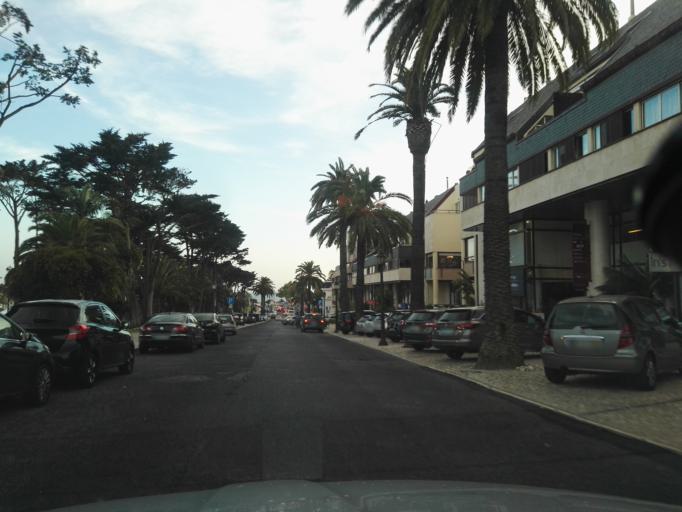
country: PT
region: Lisbon
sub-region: Cascais
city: Estoril
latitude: 38.7065
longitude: -9.3984
